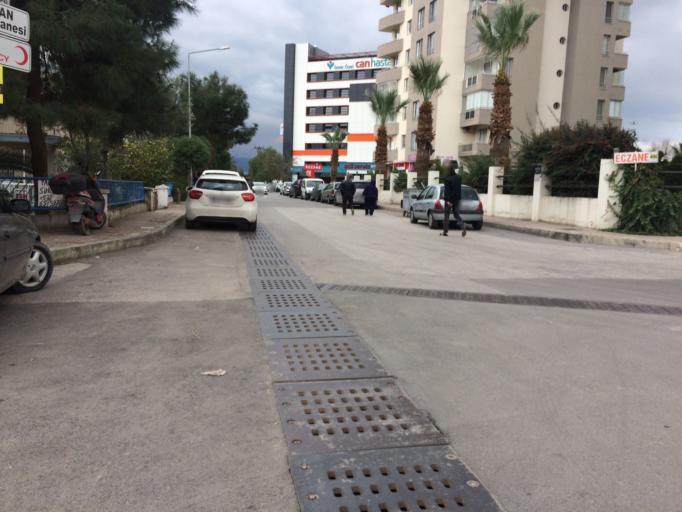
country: TR
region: Izmir
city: Karsiyaka
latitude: 38.4840
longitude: 27.0591
